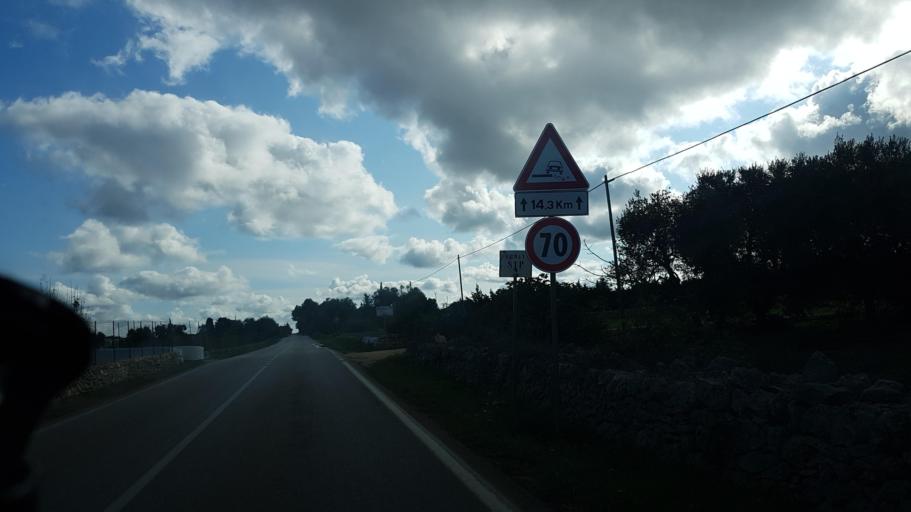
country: IT
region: Apulia
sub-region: Provincia di Brindisi
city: San Michele Salentino
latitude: 40.6702
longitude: 17.5975
